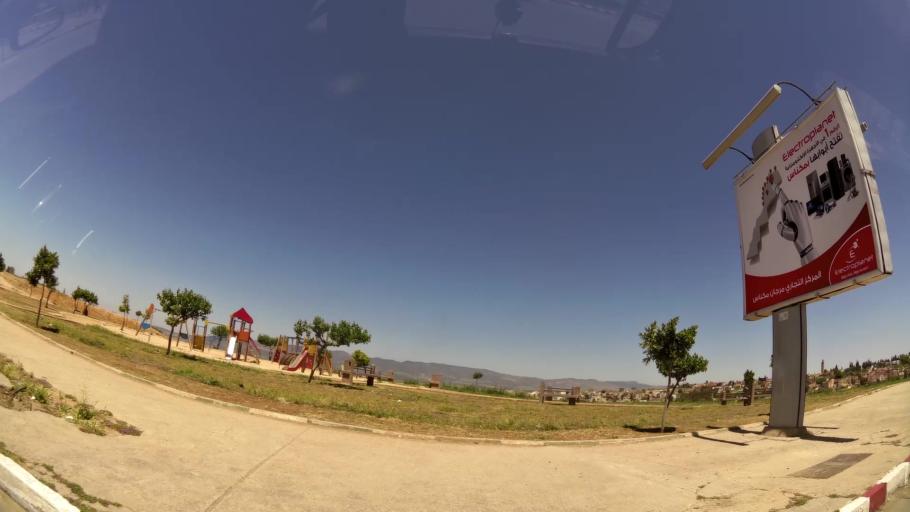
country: MA
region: Meknes-Tafilalet
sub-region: Meknes
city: Meknes
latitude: 33.9044
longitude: -5.5721
